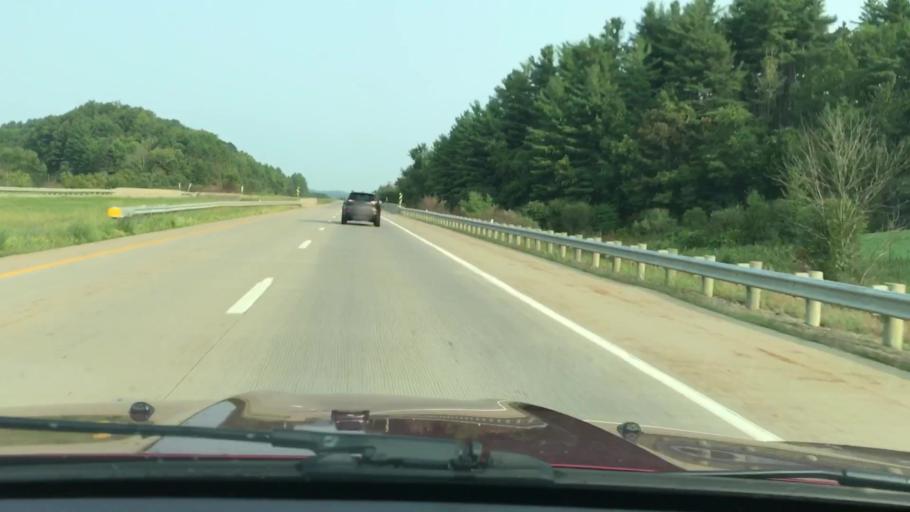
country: US
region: Ohio
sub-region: Noble County
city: Caldwell
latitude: 39.6630
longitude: -81.4715
